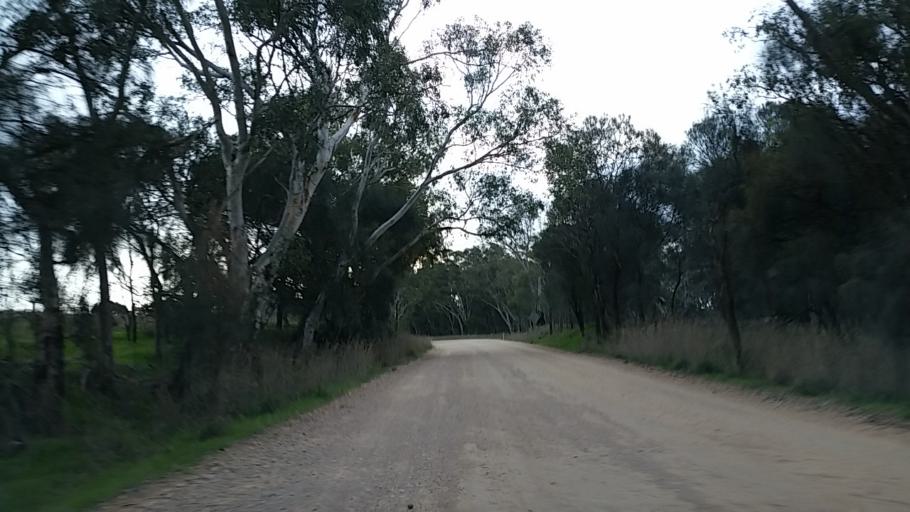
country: AU
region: South Australia
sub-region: Adelaide Hills
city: Birdwood
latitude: -34.8800
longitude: 138.9961
